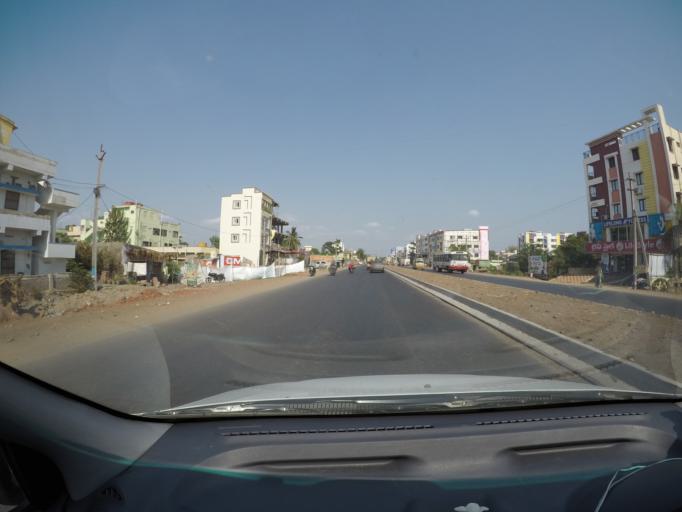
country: IN
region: Andhra Pradesh
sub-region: Krishna
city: Yanamalakuduru
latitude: 16.4777
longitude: 80.7029
